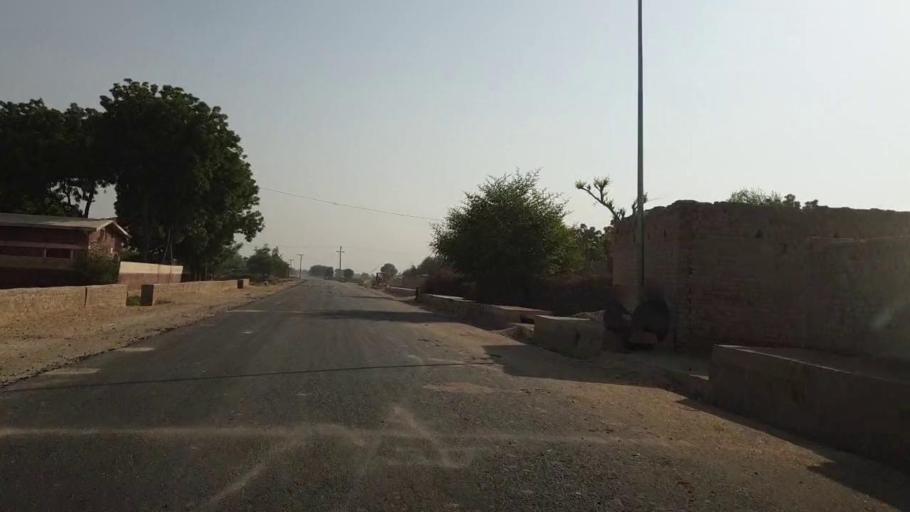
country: PK
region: Sindh
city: Bhan
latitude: 26.5353
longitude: 67.7884
